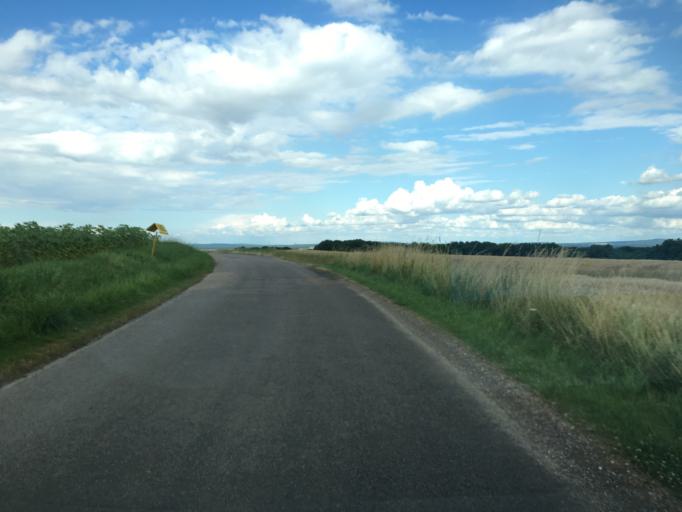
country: FR
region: Bourgogne
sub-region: Departement de l'Yonne
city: Fleury-la-Vallee
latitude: 47.8755
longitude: 3.4853
